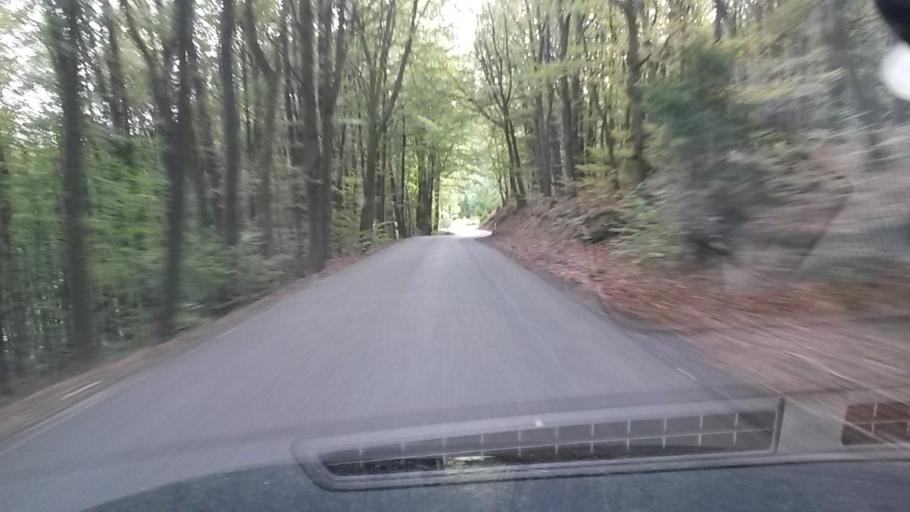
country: DE
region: North Rhine-Westphalia
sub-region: Regierungsbezirk Arnsberg
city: Herscheid
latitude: 51.1929
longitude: 7.7500
